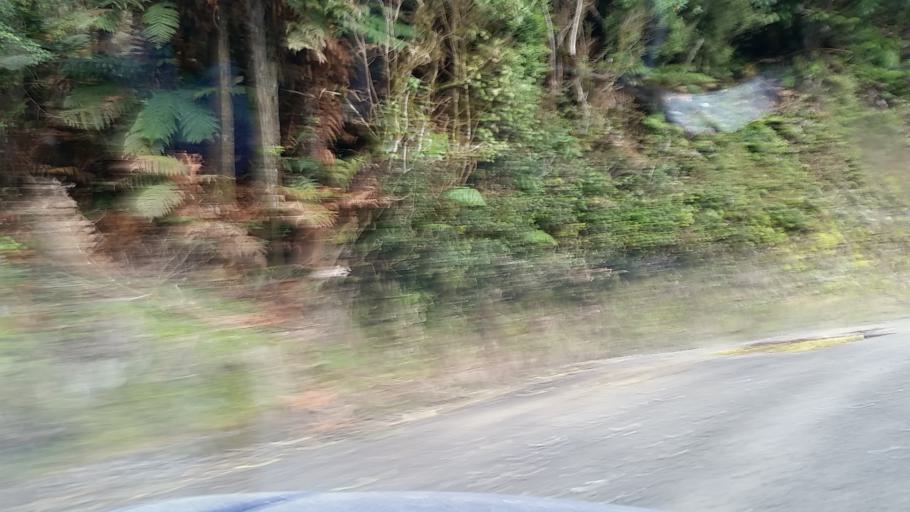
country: NZ
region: Taranaki
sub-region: South Taranaki District
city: Eltham
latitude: -39.1707
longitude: 174.6260
